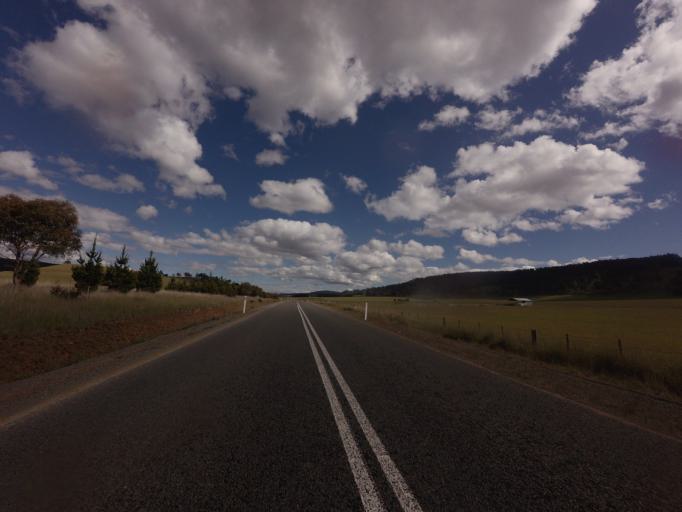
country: AU
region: Tasmania
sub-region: Brighton
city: Bridgewater
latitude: -42.4278
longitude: 147.3122
